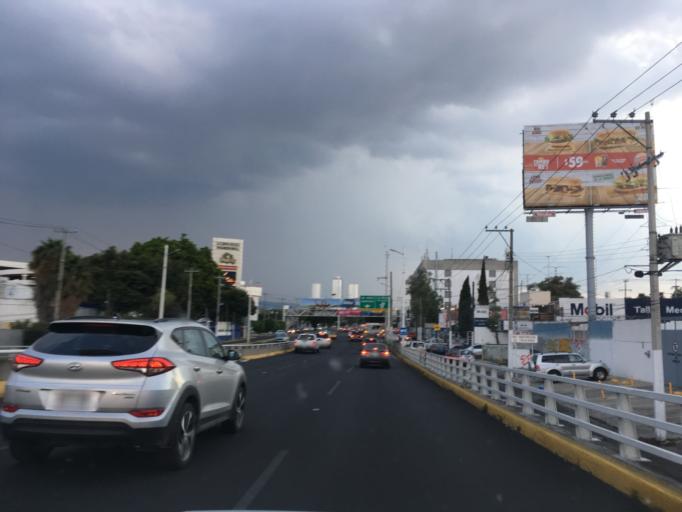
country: MX
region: Jalisco
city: Guadalajara
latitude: 20.6748
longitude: -103.4016
